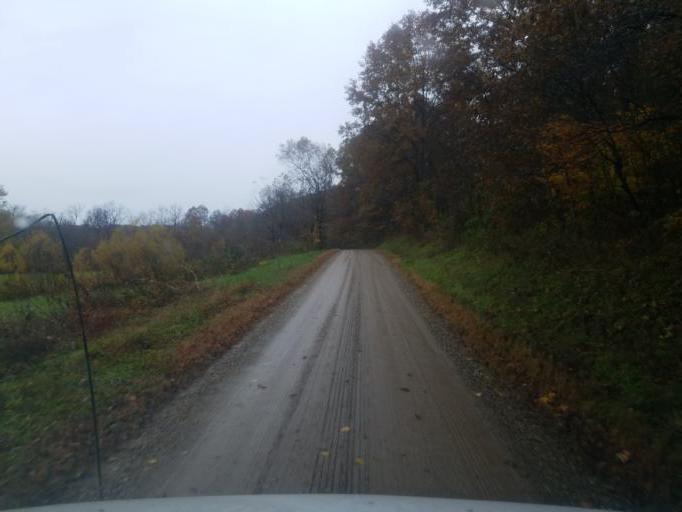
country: US
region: Ohio
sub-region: Washington County
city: Beverly
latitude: 39.4583
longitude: -81.7739
